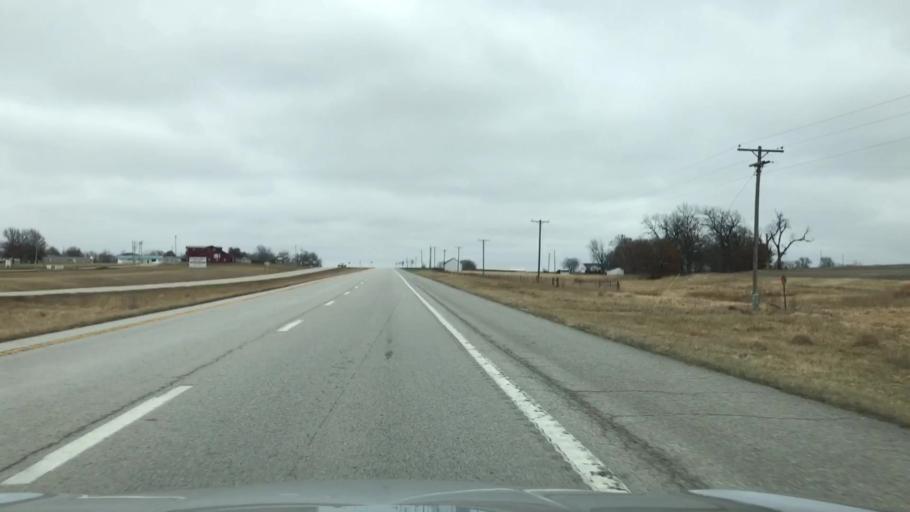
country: US
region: Missouri
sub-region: Livingston County
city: Chillicothe
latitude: 39.7753
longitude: -93.5255
